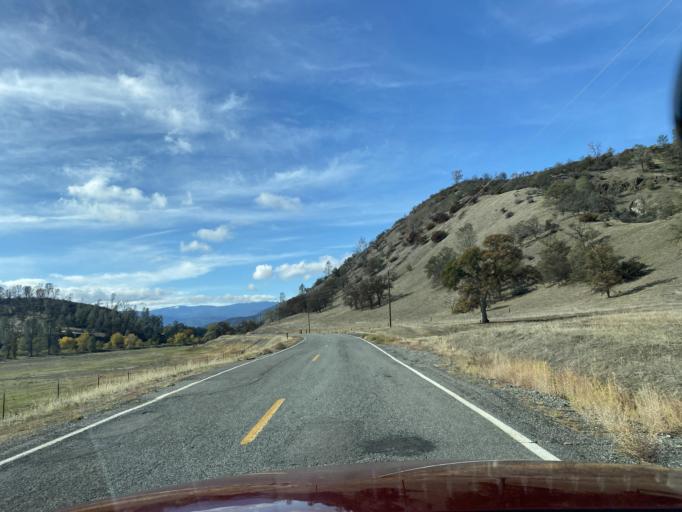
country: US
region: California
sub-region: Glenn County
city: Willows
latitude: 39.4243
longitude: -122.5307
